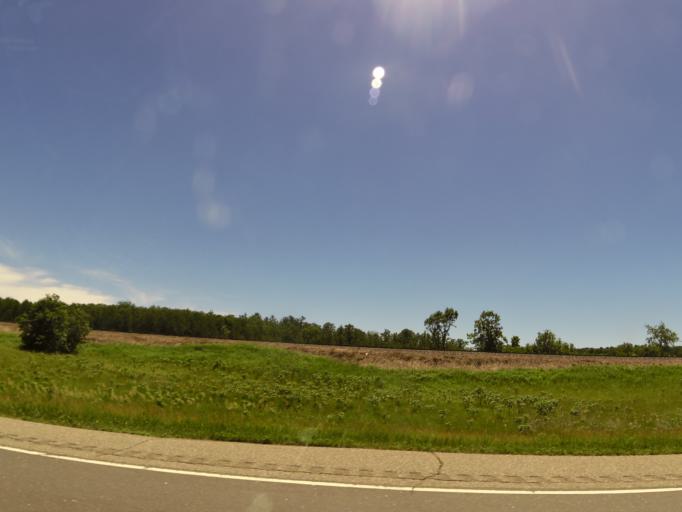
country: US
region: Minnesota
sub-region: Wadena County
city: Wadena
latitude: 46.4659
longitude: -95.2143
